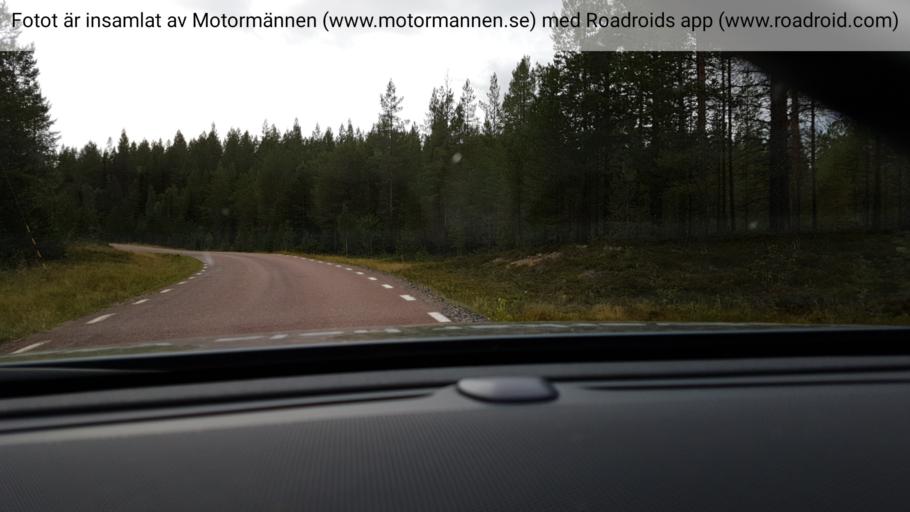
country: NO
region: Hedmark
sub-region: Trysil
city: Innbygda
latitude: 61.6558
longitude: 12.7320
